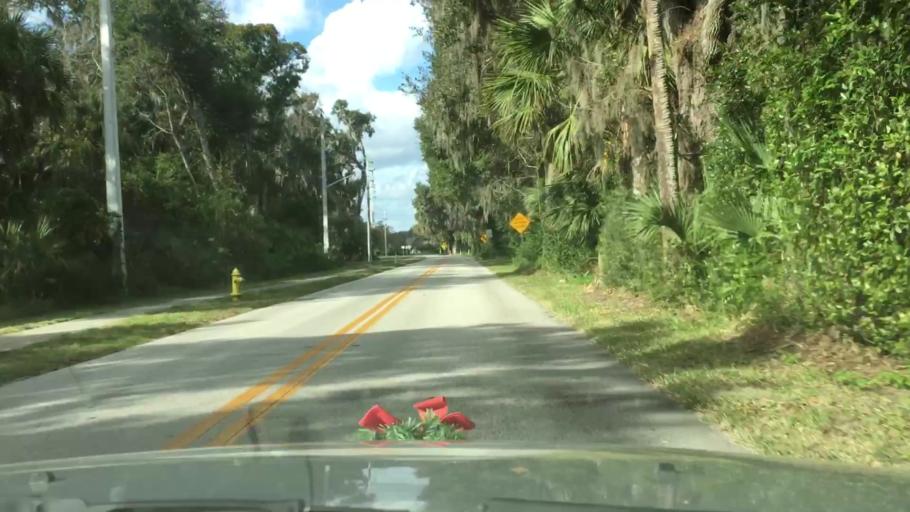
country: US
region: Florida
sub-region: Volusia County
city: Ormond Beach
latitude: 29.2862
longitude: -81.0717
